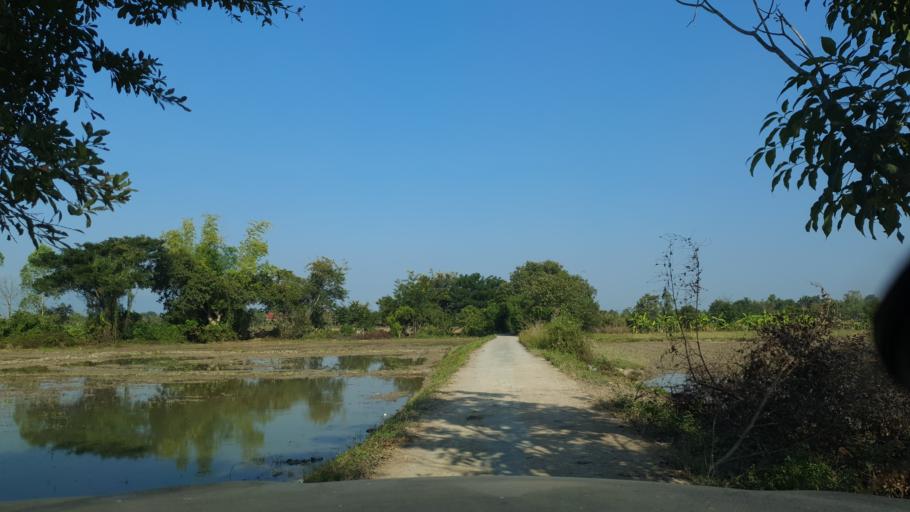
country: TH
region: Chiang Mai
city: Saraphi
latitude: 18.6899
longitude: 99.0855
